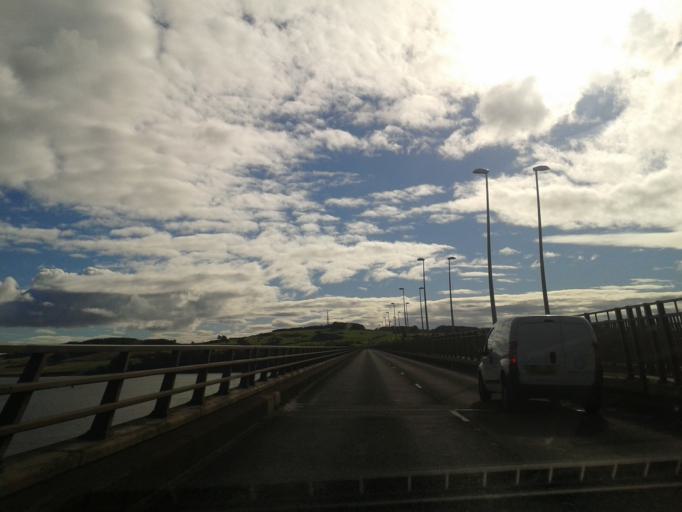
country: GB
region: Scotland
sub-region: Fife
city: Newport-On-Tay
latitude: 56.4538
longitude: -2.9500
